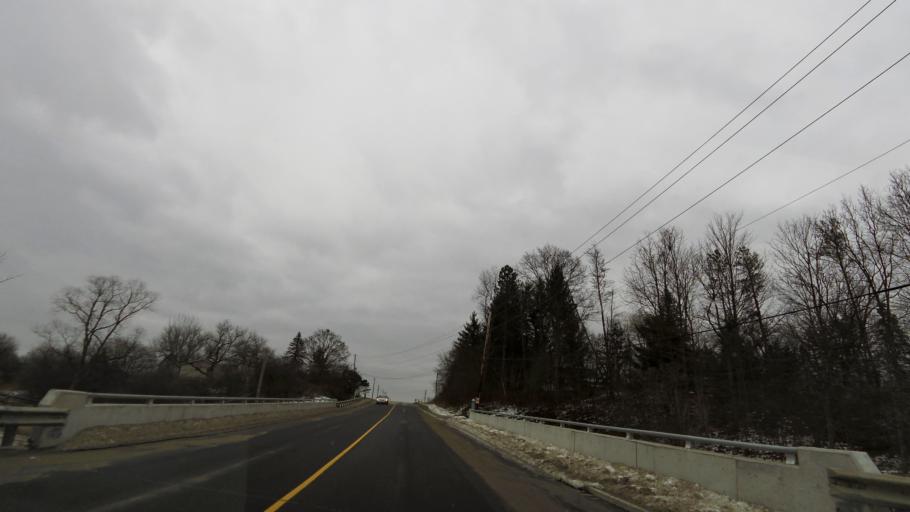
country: CA
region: Ontario
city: Brantford
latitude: 43.0639
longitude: -80.1049
